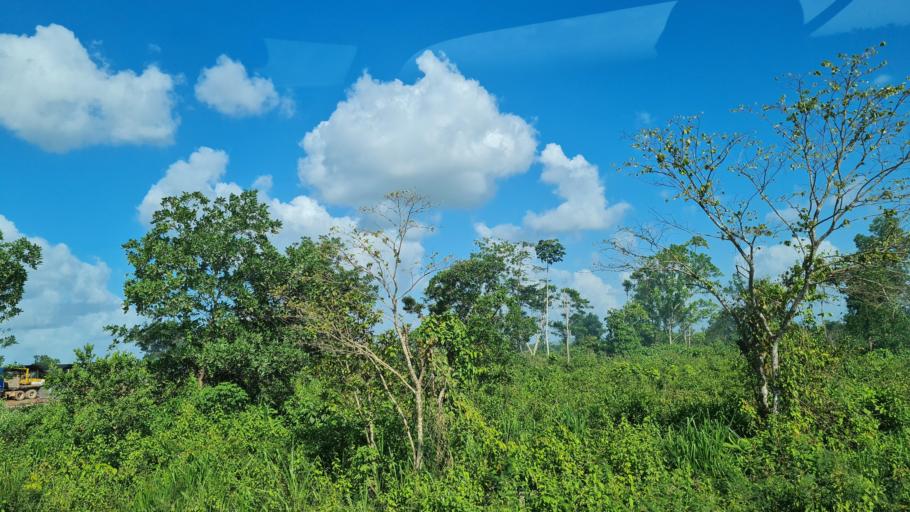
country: NI
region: Atlantico Norte (RAAN)
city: Bonanza
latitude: 13.9960
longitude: -84.1694
